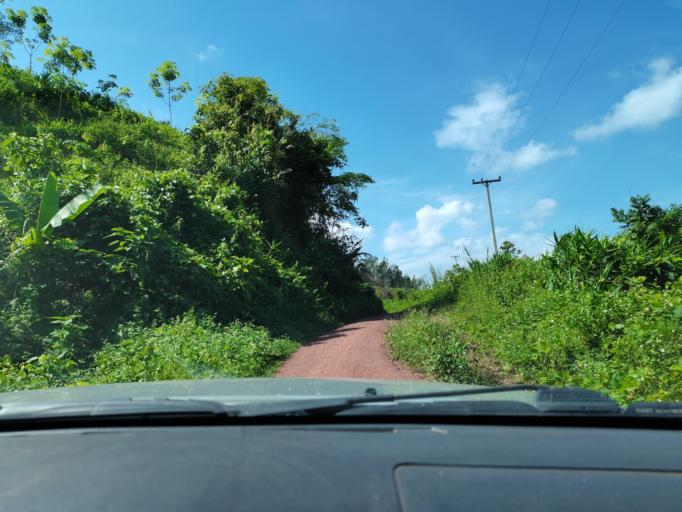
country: LA
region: Loungnamtha
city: Muang Nale
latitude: 20.5640
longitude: 101.0564
